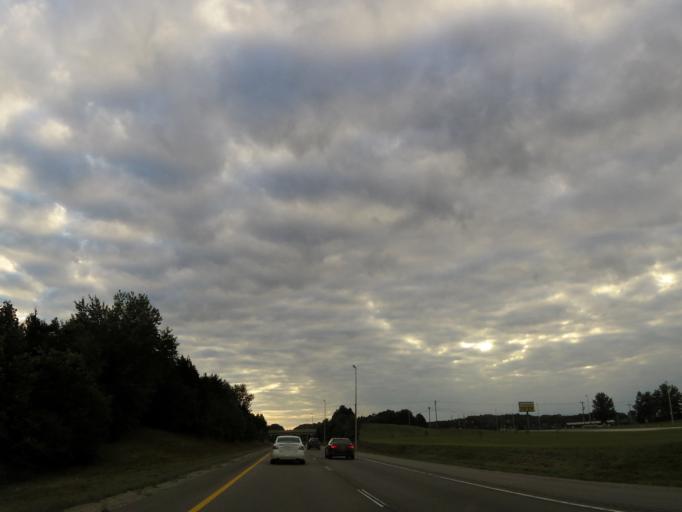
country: US
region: Tennessee
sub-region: Putnam County
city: Cookeville
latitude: 36.1368
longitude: -85.5252
